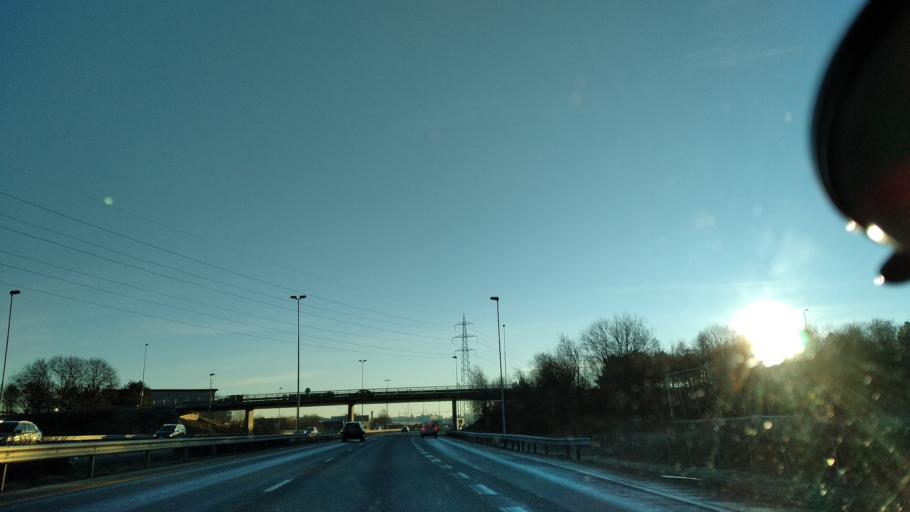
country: NO
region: Rogaland
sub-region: Sandnes
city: Sandnes
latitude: 58.8875
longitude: 5.7172
